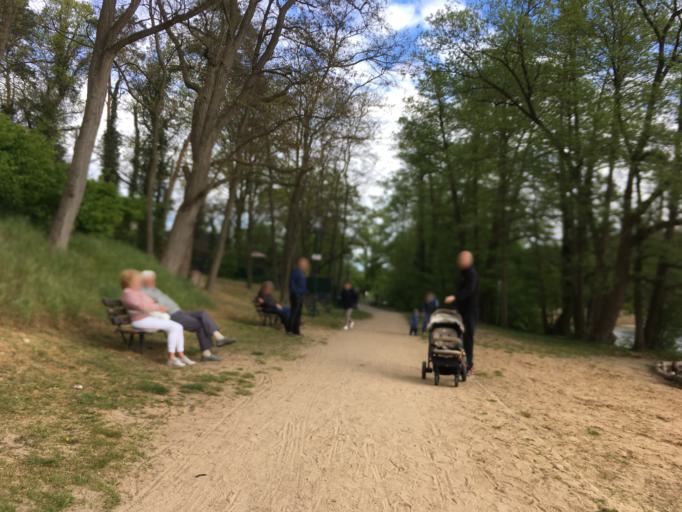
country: DE
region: Brandenburg
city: Rudnitz
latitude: 52.7610
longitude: 13.5565
